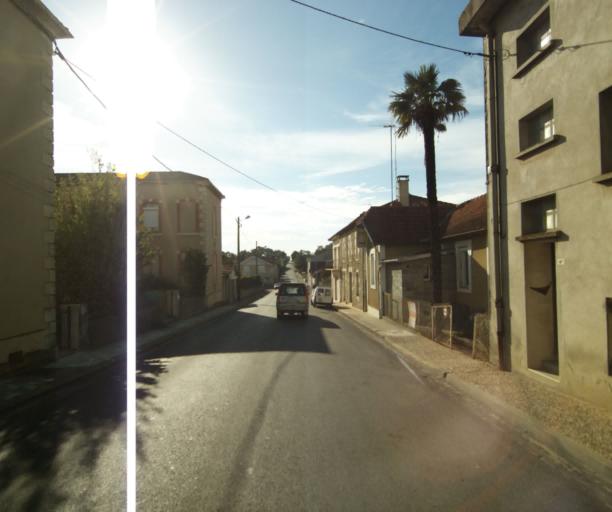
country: FR
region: Midi-Pyrenees
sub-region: Departement du Gers
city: Eauze
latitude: 43.8601
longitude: 0.0975
